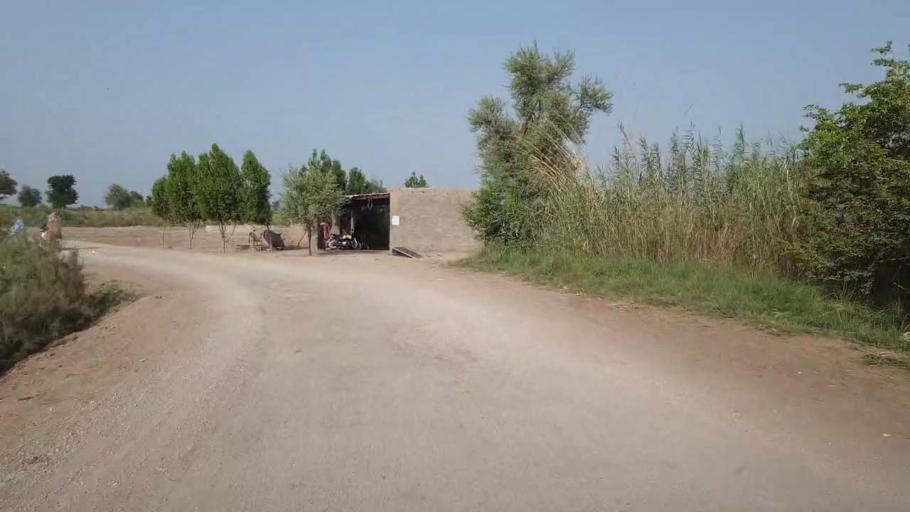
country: PK
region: Sindh
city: Daur
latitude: 26.3482
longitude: 68.1715
